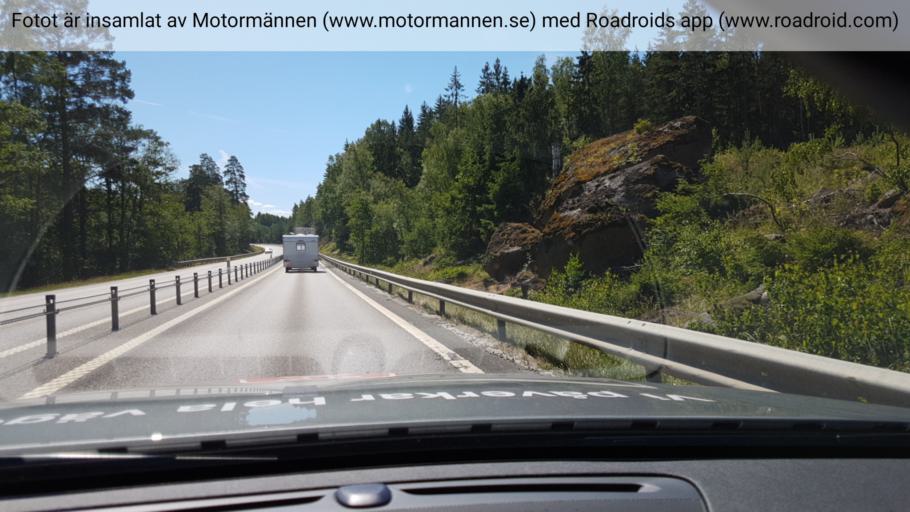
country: SE
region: OEstergoetland
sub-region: Norrkopings Kommun
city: Jursla
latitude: 58.7445
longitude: 16.1728
